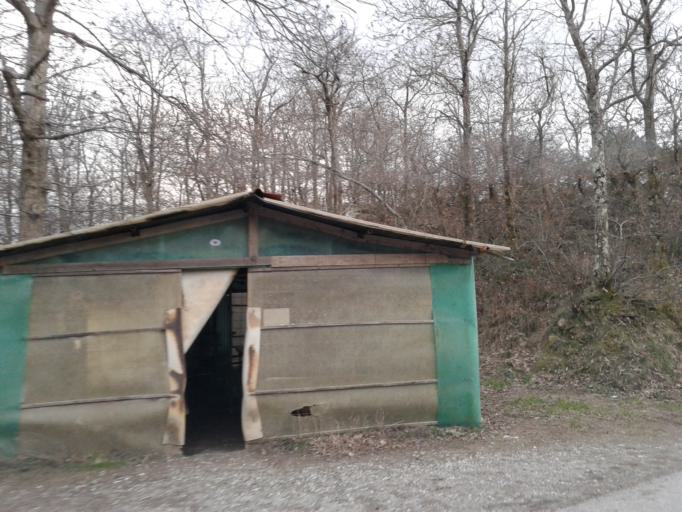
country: IT
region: Tuscany
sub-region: Province of Pisa
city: Calci
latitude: 43.7600
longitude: 10.5320
